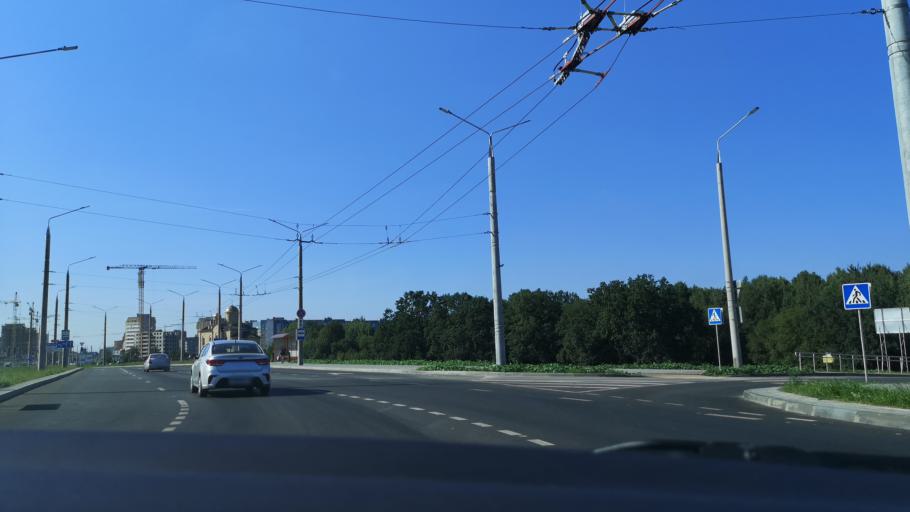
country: BY
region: Grodnenskaya
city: Hrodna
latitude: 53.6500
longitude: 23.8606
